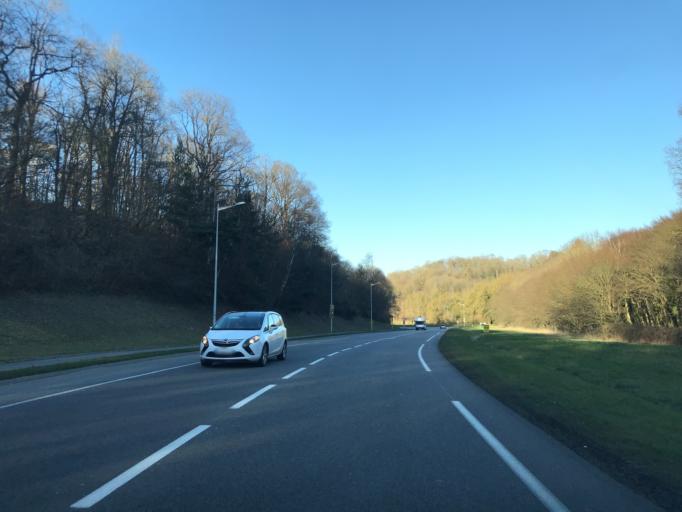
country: FR
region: Haute-Normandie
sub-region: Departement de l'Eure
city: Evreux
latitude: 49.0129
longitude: 1.1421
